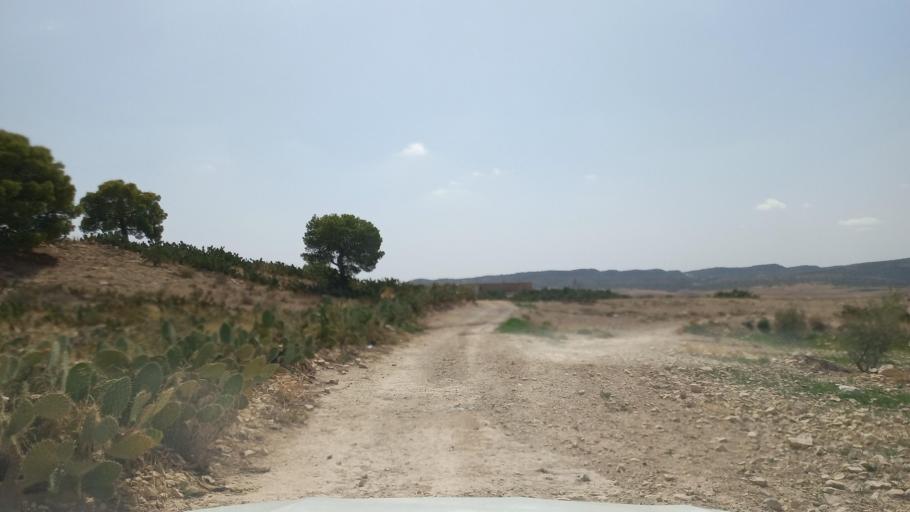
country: TN
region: Al Qasrayn
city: Sbiba
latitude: 35.4062
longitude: 8.9710
